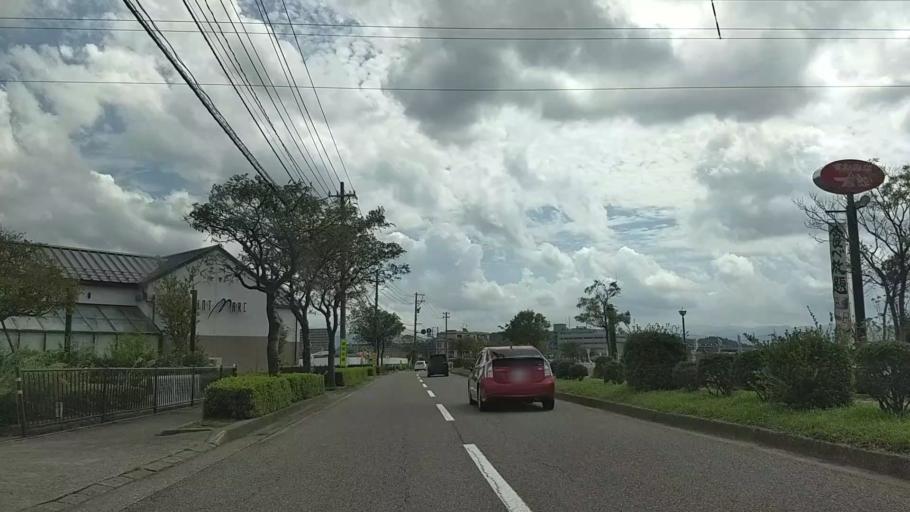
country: JP
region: Ishikawa
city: Kanazawa-shi
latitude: 36.5976
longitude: 136.6612
